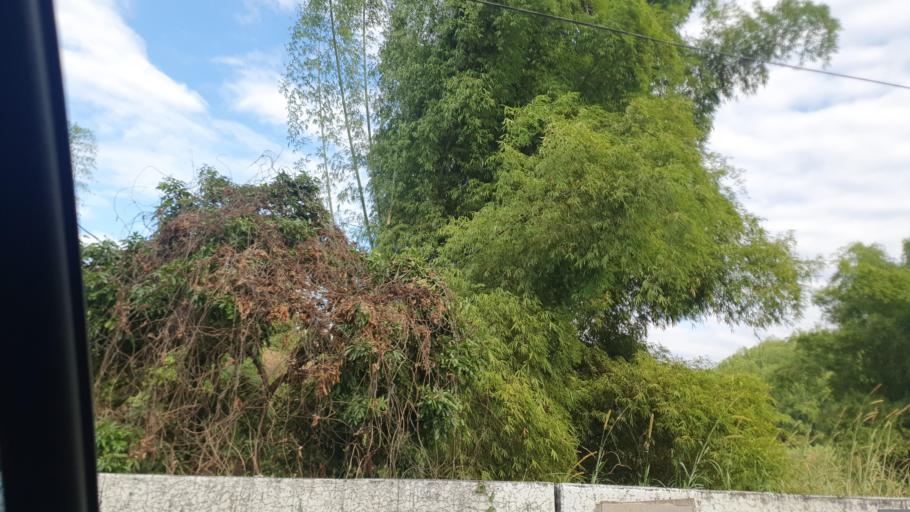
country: TW
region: Taiwan
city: Yujing
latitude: 23.0166
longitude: 120.4161
